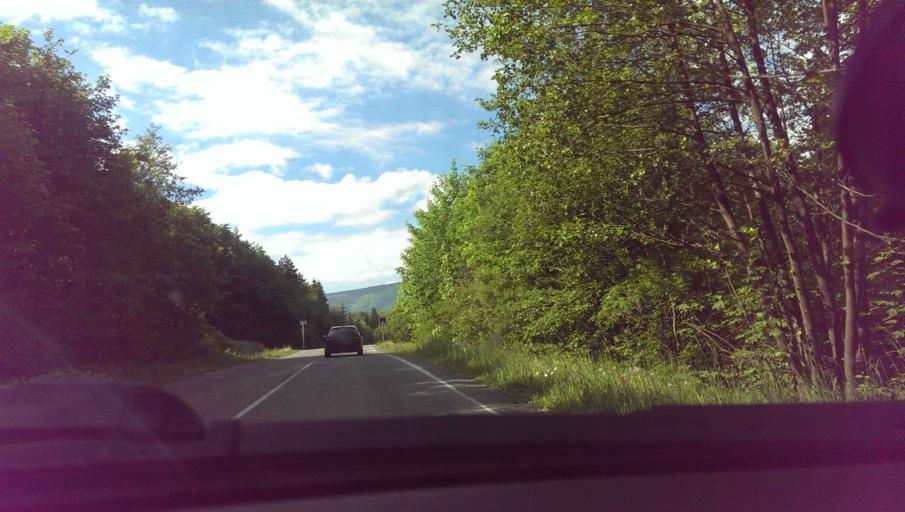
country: CZ
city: Kuncice pod Ondrejnikem
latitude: 49.5439
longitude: 18.2534
